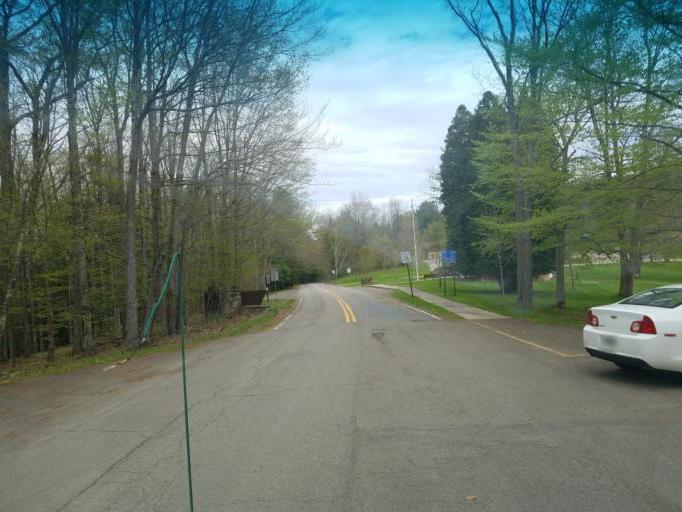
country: US
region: Pennsylvania
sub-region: Tioga County
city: Wellsboro
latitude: 41.6978
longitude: -77.4524
